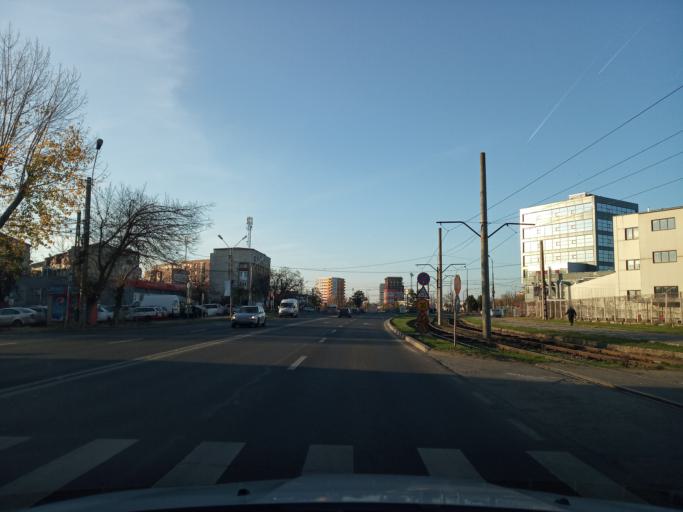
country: RO
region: Timis
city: Timisoara
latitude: 45.7315
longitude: 21.2622
